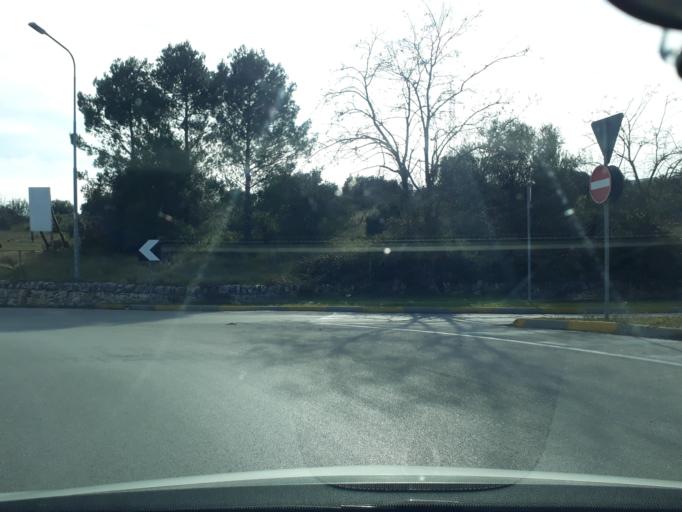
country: IT
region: Apulia
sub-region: Provincia di Bari
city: Locorotondo
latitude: 40.7546
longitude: 17.3438
